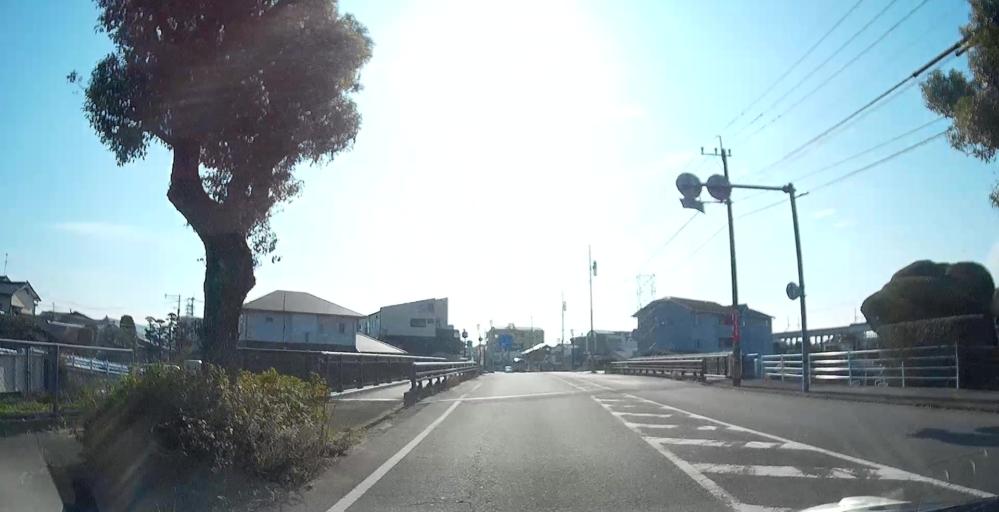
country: JP
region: Kumamoto
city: Kumamoto
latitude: 32.7458
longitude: 130.6827
